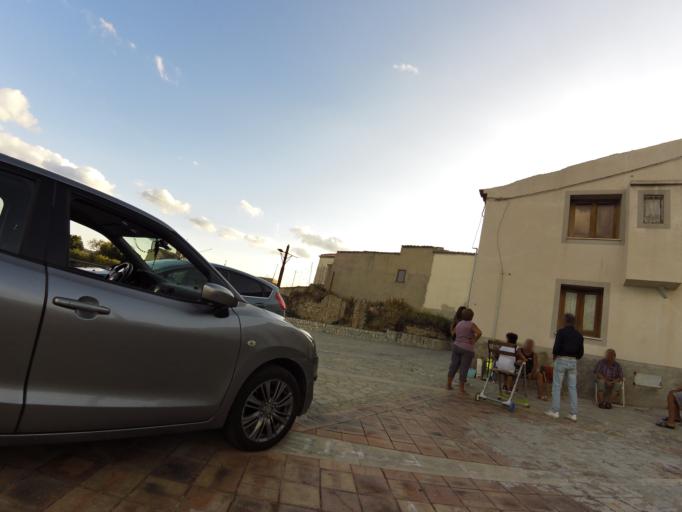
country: IT
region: Calabria
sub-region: Provincia di Reggio Calabria
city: Caulonia
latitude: 38.3804
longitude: 16.4097
